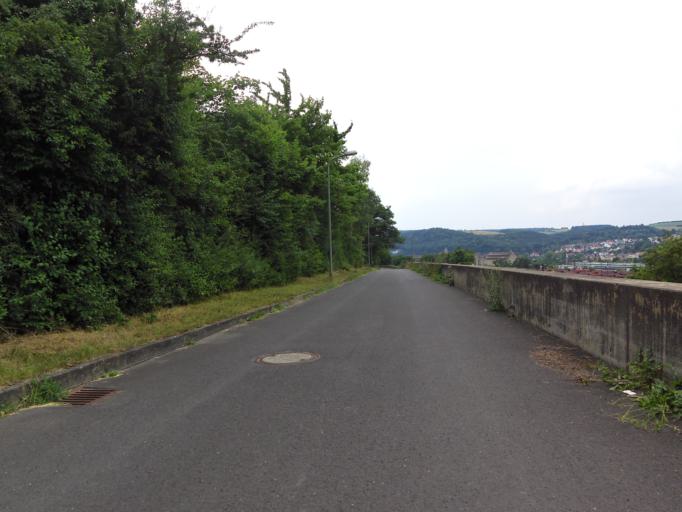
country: DE
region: Bavaria
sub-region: Regierungsbezirk Unterfranken
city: Veitshochheim
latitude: 49.8216
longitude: 9.8786
